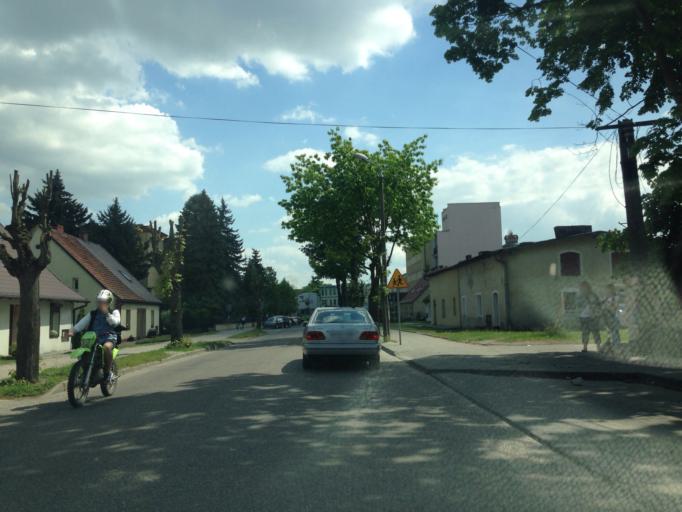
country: PL
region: Kujawsko-Pomorskie
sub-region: Powiat brodnicki
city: Brodnica
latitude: 53.2615
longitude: 19.3962
